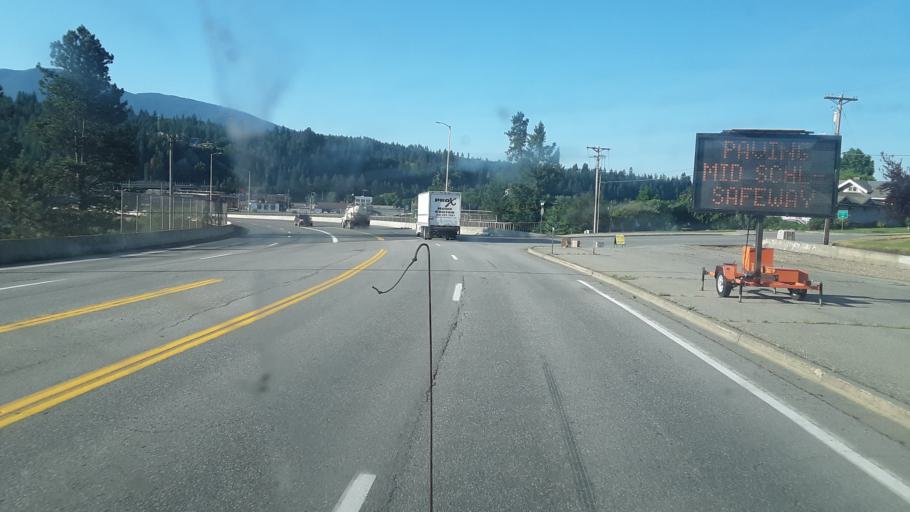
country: US
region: Idaho
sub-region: Boundary County
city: Bonners Ferry
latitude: 48.7022
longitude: -116.3139
